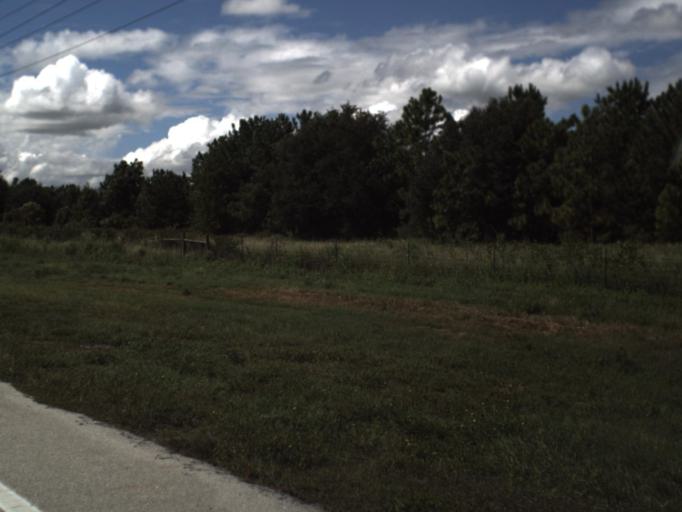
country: US
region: Florida
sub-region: Polk County
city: Mulberry
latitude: 27.7658
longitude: -81.9917
